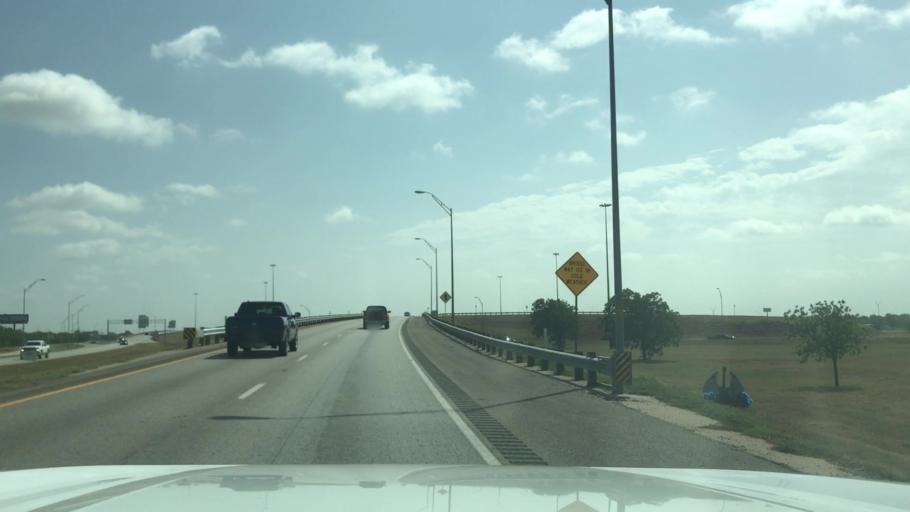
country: US
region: Texas
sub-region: Taylor County
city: Abilene
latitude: 32.4813
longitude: -99.7760
